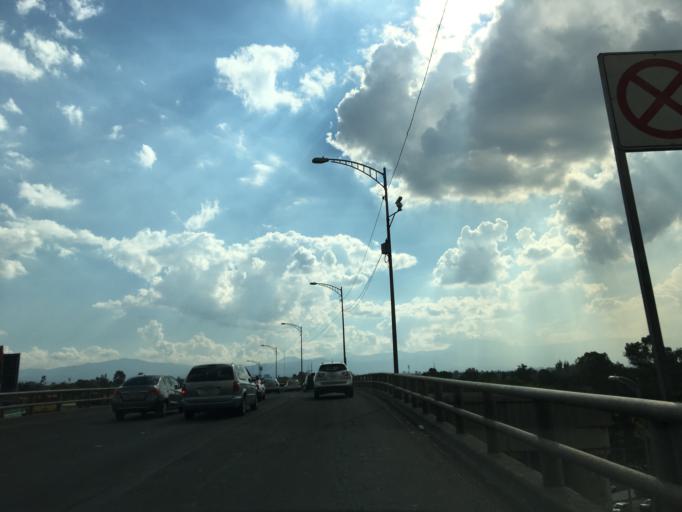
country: MX
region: Mexico City
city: Mexico City
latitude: 19.4277
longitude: -99.1112
